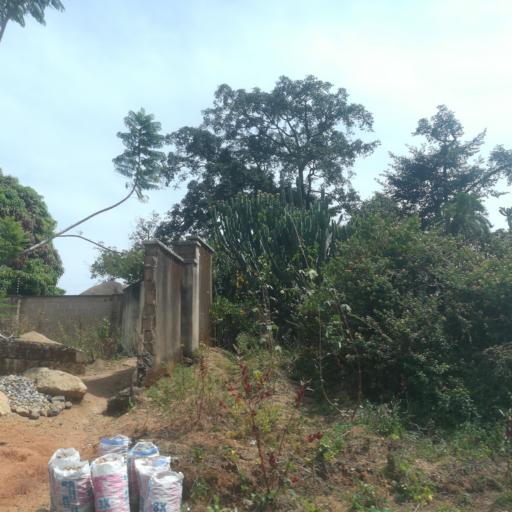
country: NG
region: Plateau
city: Jos
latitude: 9.9076
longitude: 8.8763
